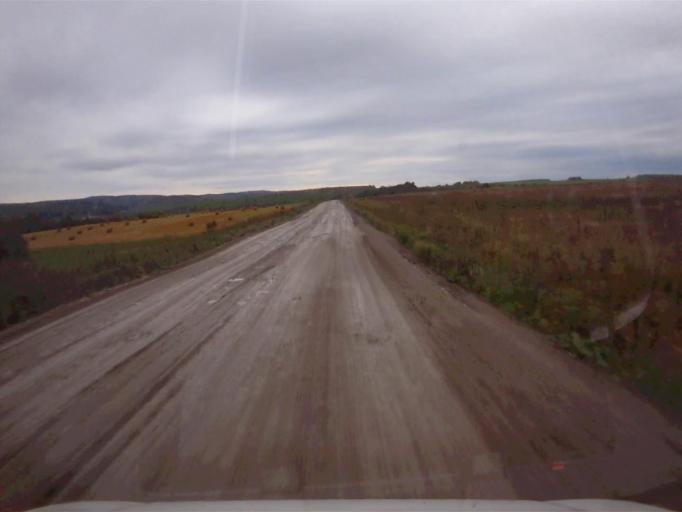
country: RU
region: Sverdlovsk
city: Mikhaylovsk
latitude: 56.1807
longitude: 59.1917
